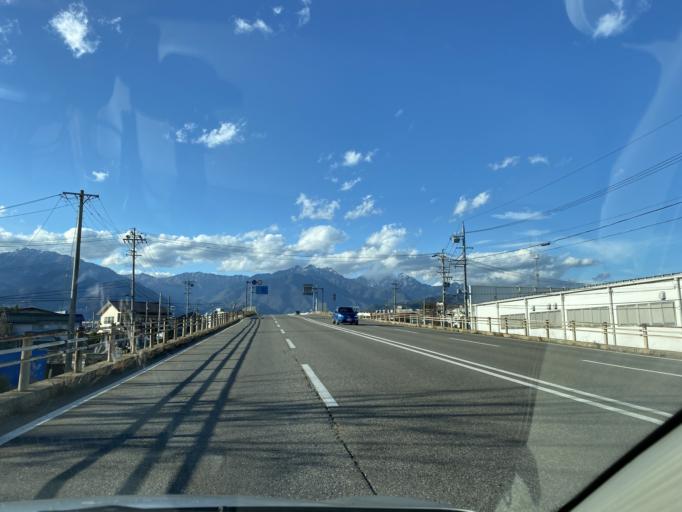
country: JP
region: Nagano
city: Omachi
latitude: 36.4968
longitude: 137.8617
